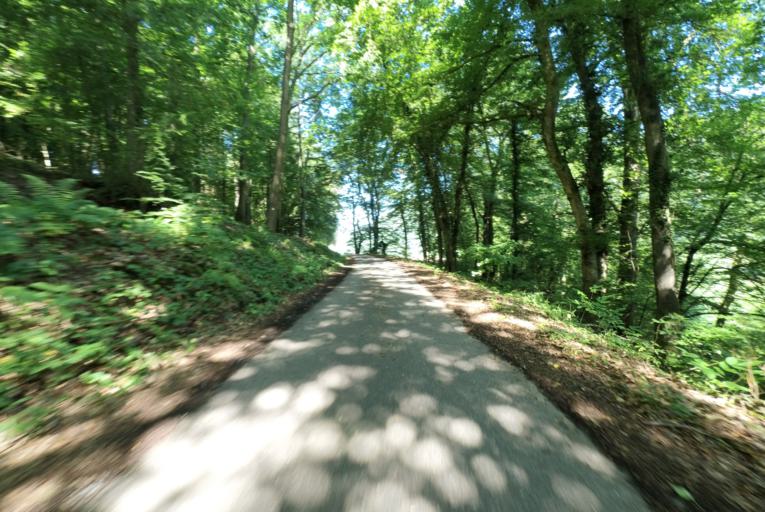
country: DE
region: Baden-Wuerttemberg
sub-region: Karlsruhe Region
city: Neckargerach
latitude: 49.4000
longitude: 9.0641
